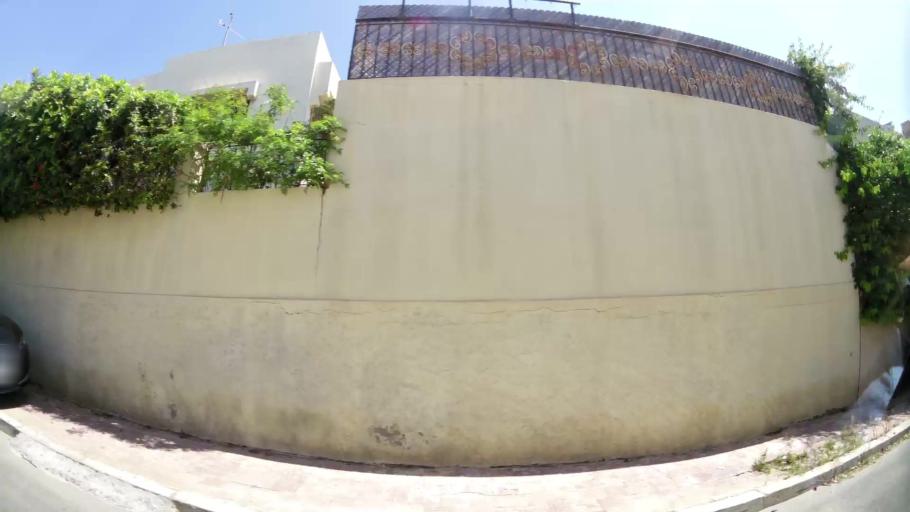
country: MA
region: Souss-Massa-Draa
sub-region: Agadir-Ida-ou-Tnan
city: Agadir
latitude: 30.4351
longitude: -9.5837
